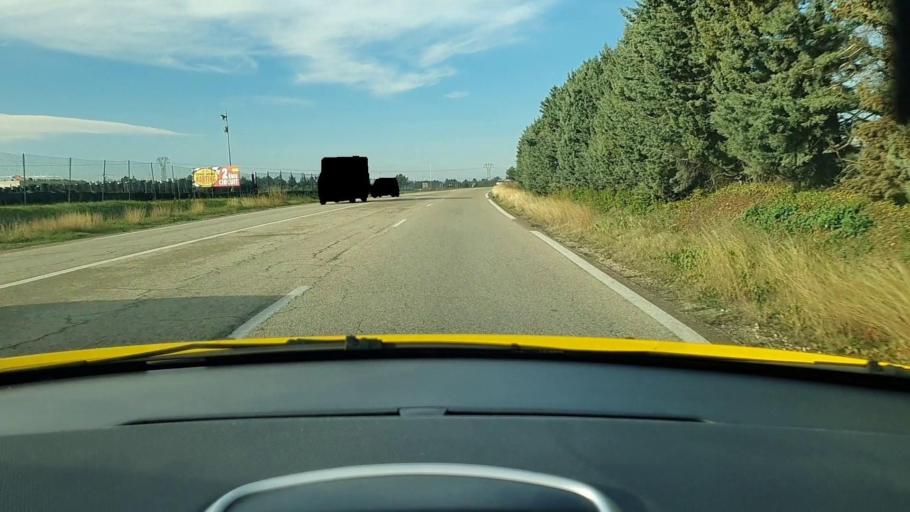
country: FR
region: Languedoc-Roussillon
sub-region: Departement du Gard
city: Comps
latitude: 43.8197
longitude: 4.6059
